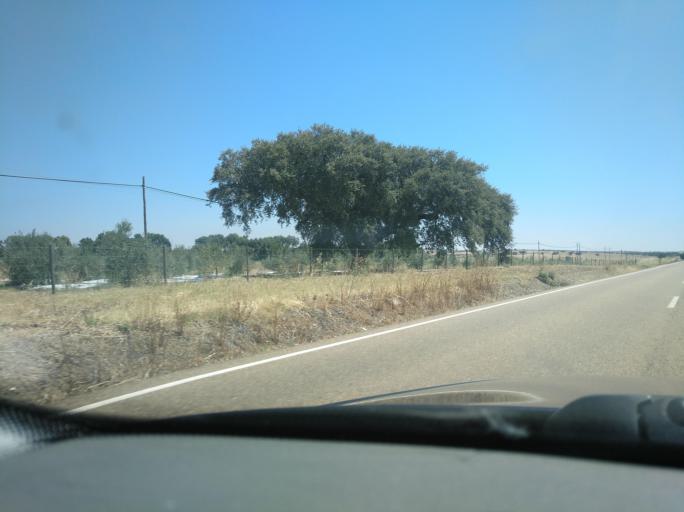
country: ES
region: Extremadura
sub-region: Provincia de Badajoz
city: Olivenza
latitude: 38.7033
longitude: -7.1639
